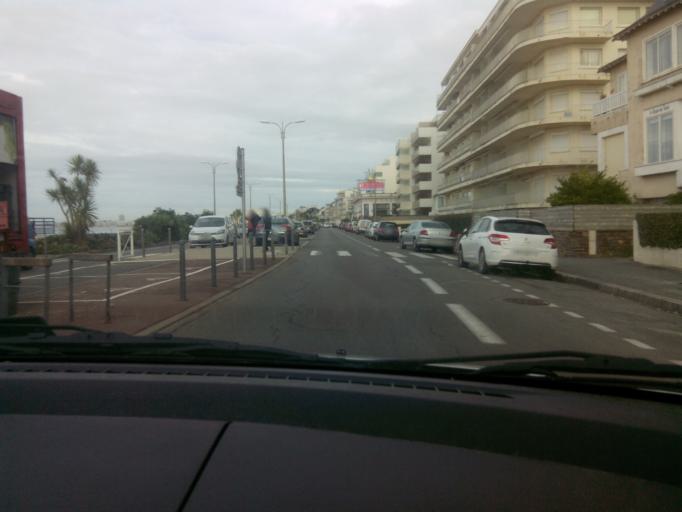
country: FR
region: Pays de la Loire
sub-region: Departement de la Loire-Atlantique
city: Pornichet
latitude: 47.2658
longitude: -2.3457
